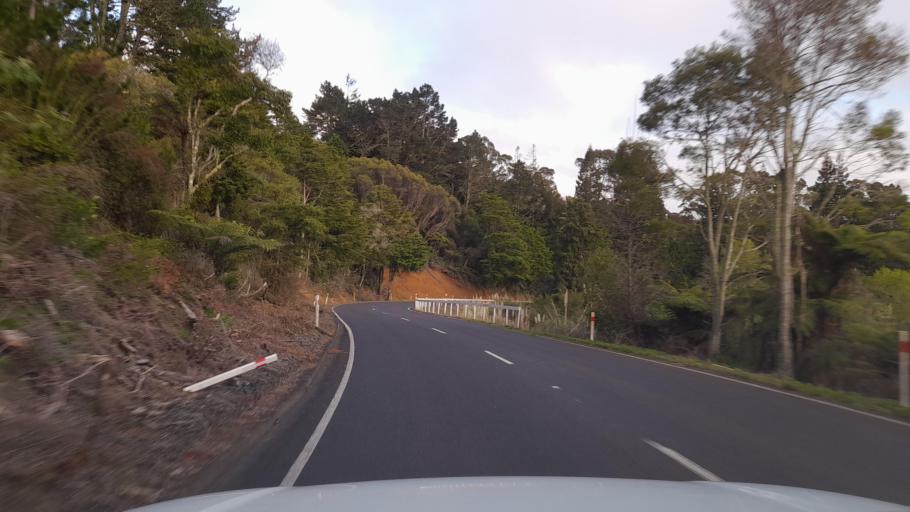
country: NZ
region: Northland
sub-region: Far North District
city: Waimate North
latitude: -35.5065
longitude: 173.8363
